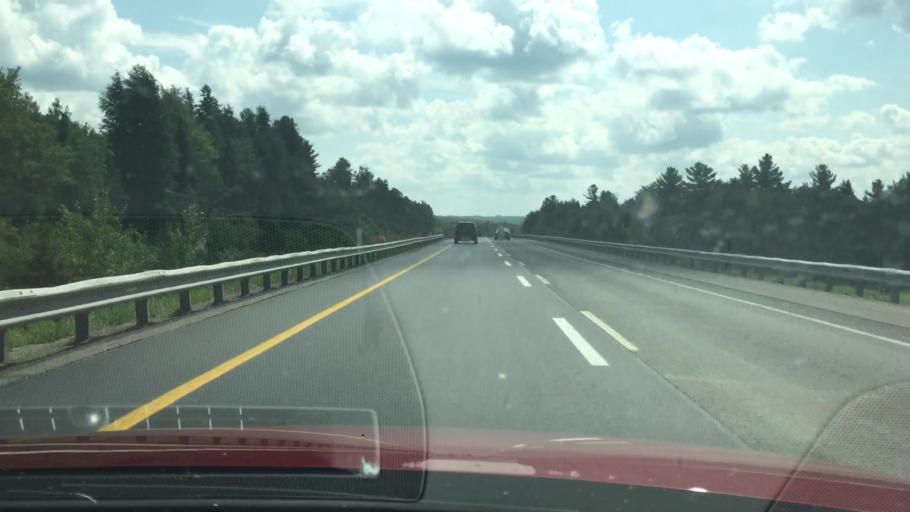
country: US
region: Maine
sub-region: Penobscot County
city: Medway
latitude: 45.6496
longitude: -68.4994
